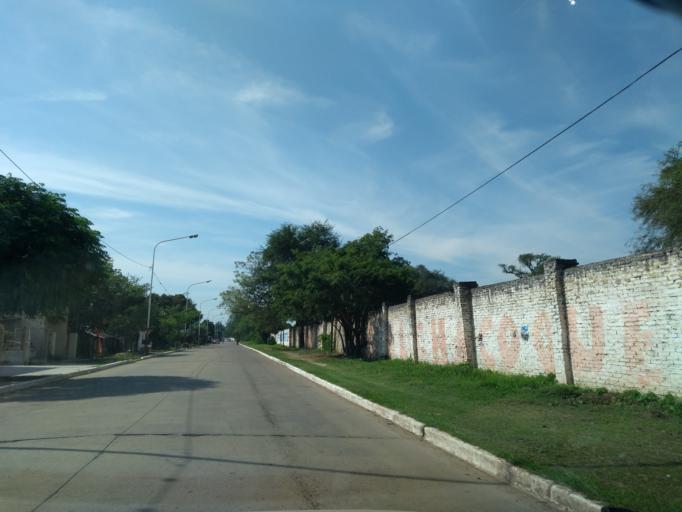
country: AR
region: Chaco
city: Resistencia
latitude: -27.4646
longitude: -58.9578
